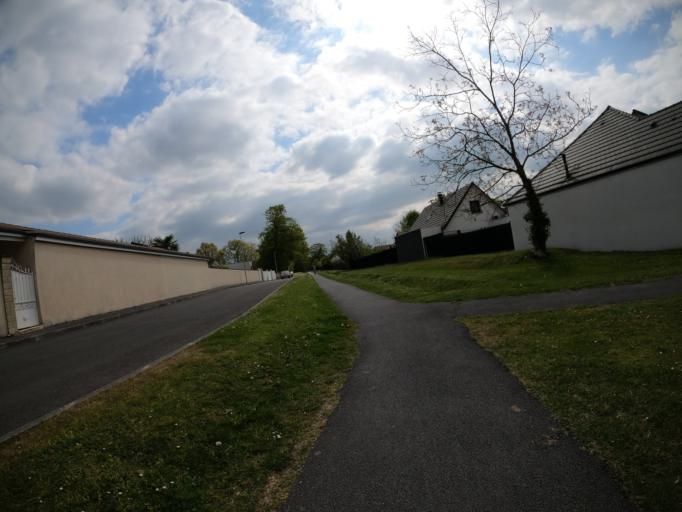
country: FR
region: Aquitaine
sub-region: Departement des Pyrenees-Atlantiques
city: Lons
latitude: 43.3251
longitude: -0.3839
